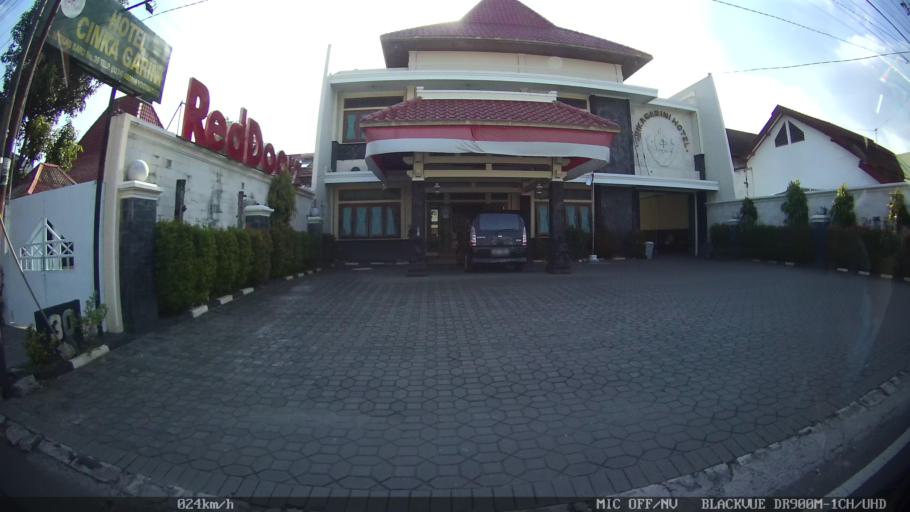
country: ID
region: Daerah Istimewa Yogyakarta
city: Yogyakarta
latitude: -7.8191
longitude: 110.3827
